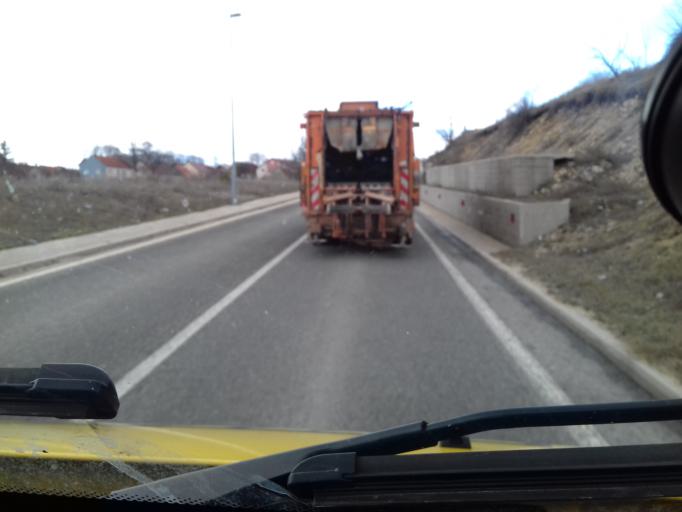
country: BA
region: Federation of Bosnia and Herzegovina
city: Tomislavgrad
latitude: 43.7296
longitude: 17.2230
